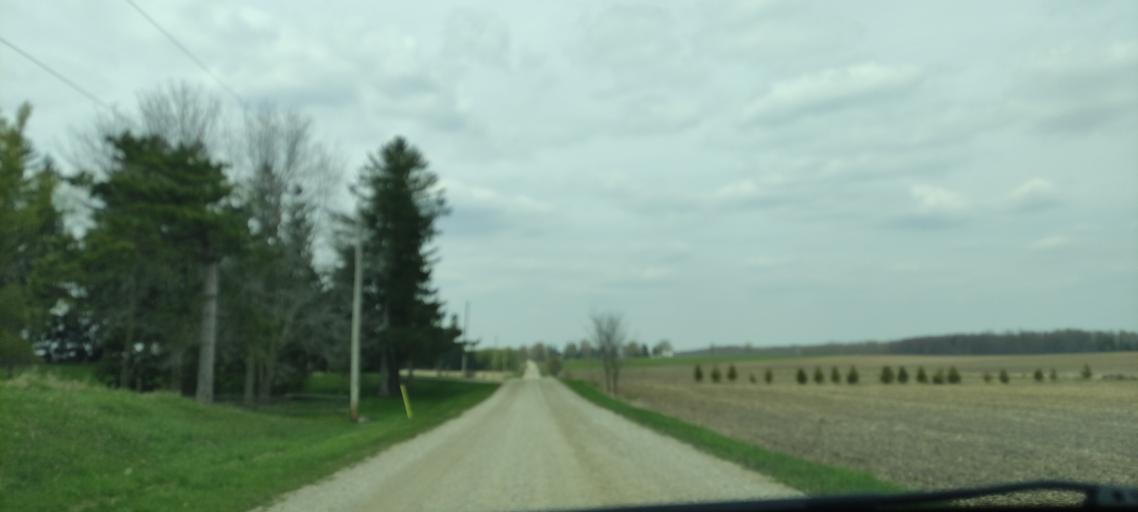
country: CA
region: Ontario
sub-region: Oxford County
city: Woodstock
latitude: 43.2795
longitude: -80.7449
